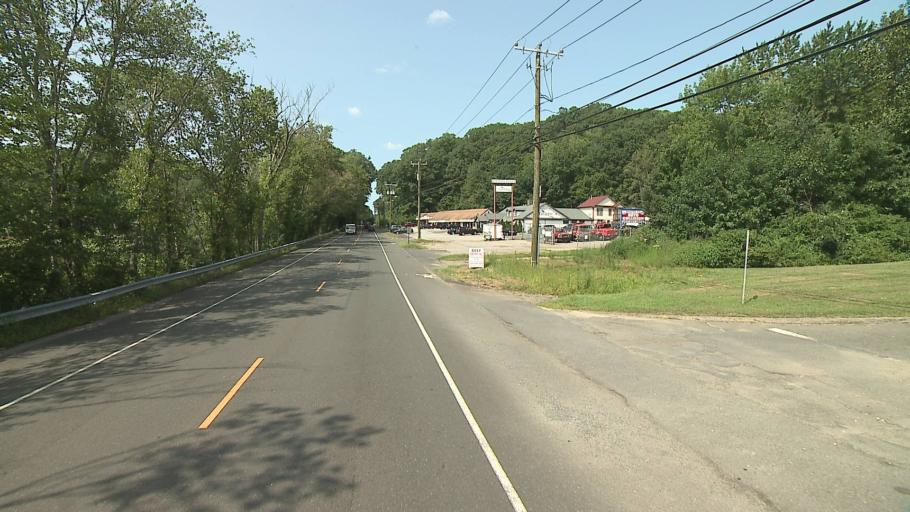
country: US
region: Connecticut
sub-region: Fairfield County
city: Trumbull
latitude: 41.3106
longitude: -73.2579
